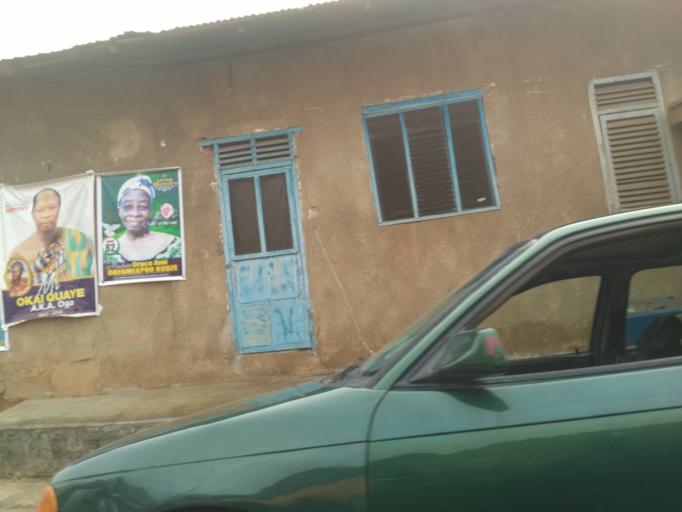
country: GH
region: Ashanti
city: Kumasi
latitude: 6.6795
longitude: -1.5927
